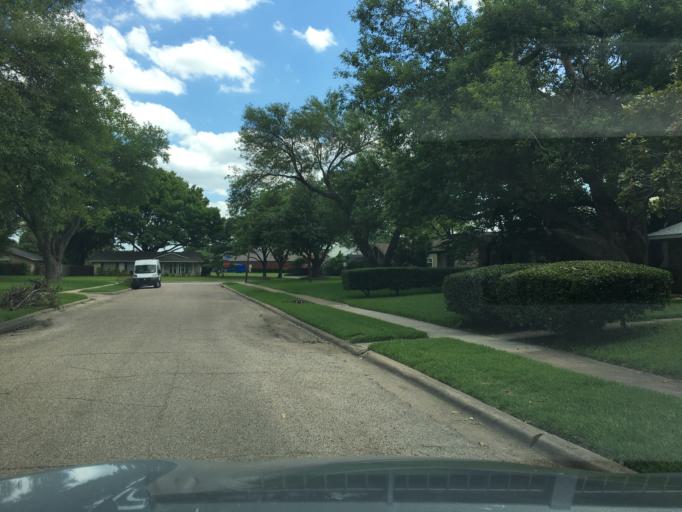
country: US
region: Texas
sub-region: Dallas County
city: Richardson
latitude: 32.9483
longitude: -96.7092
